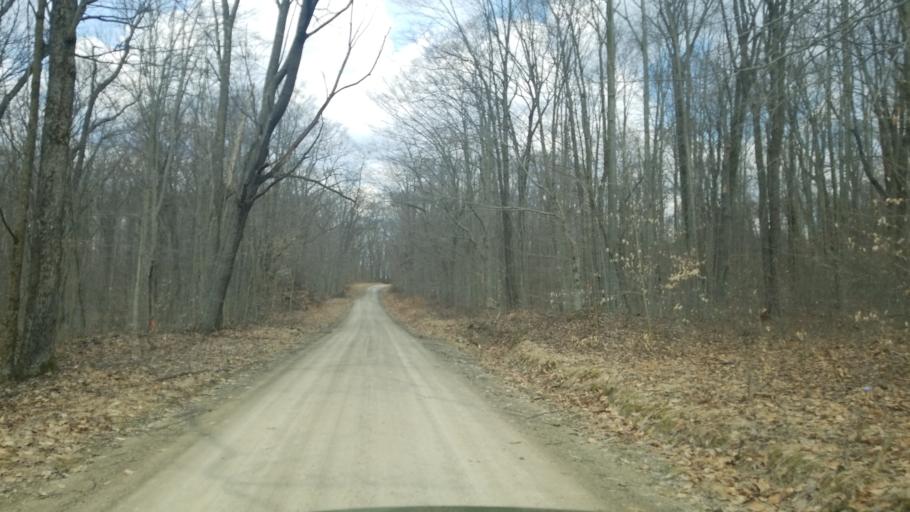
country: US
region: Pennsylvania
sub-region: Clearfield County
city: Clearfield
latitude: 41.1541
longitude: -78.5171
